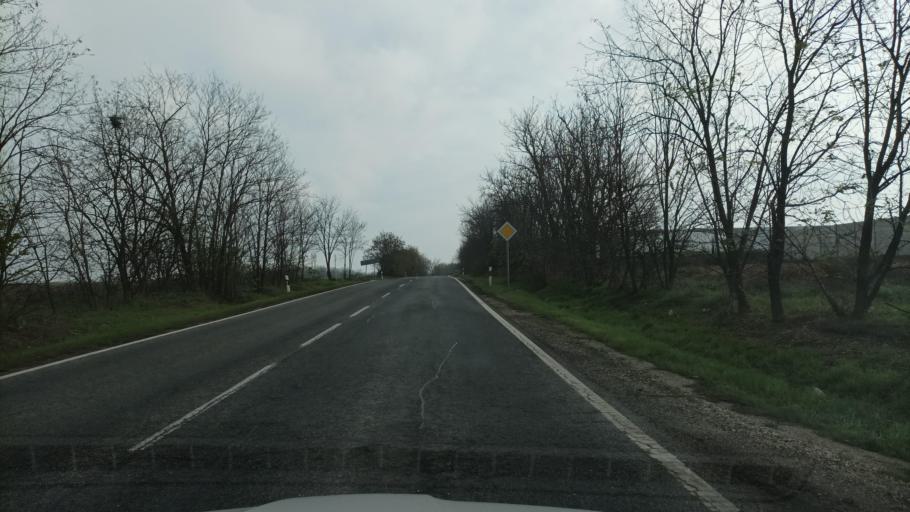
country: HU
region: Pest
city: Alsonemedi
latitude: 47.3554
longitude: 19.1589
